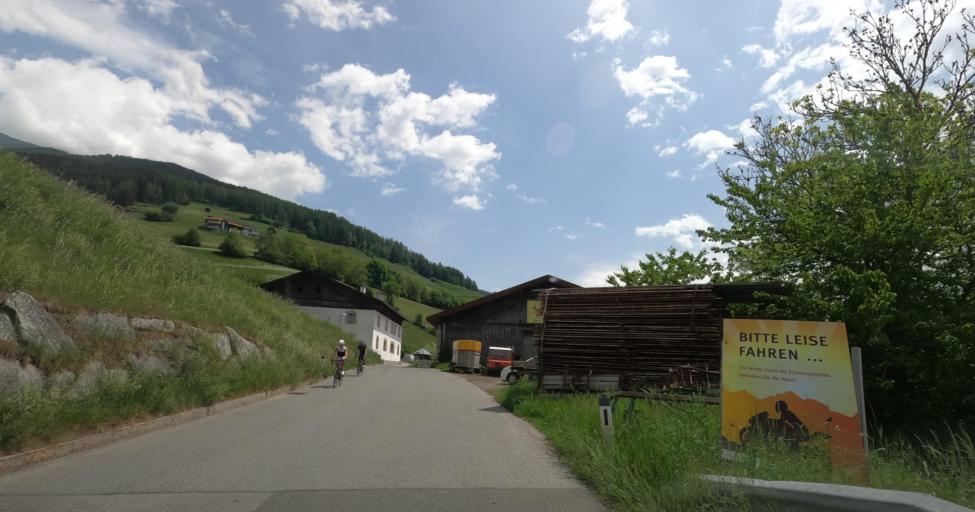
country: AT
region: Tyrol
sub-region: Politischer Bezirk Innsbruck Land
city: Ellbogen
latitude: 47.1588
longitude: 11.4527
